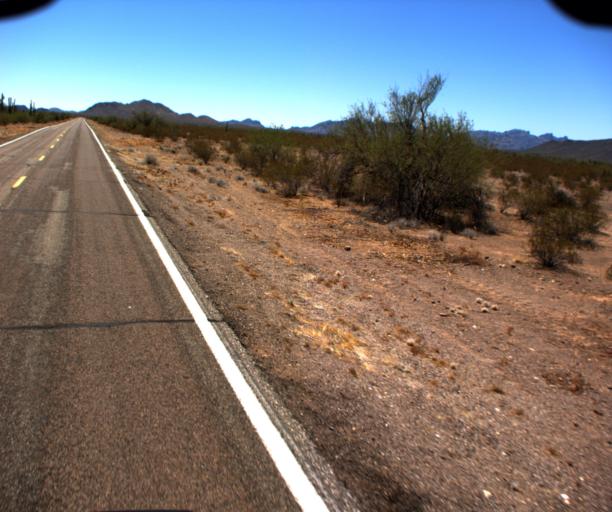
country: US
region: Arizona
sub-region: Pima County
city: Ajo
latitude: 32.2390
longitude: -112.7220
